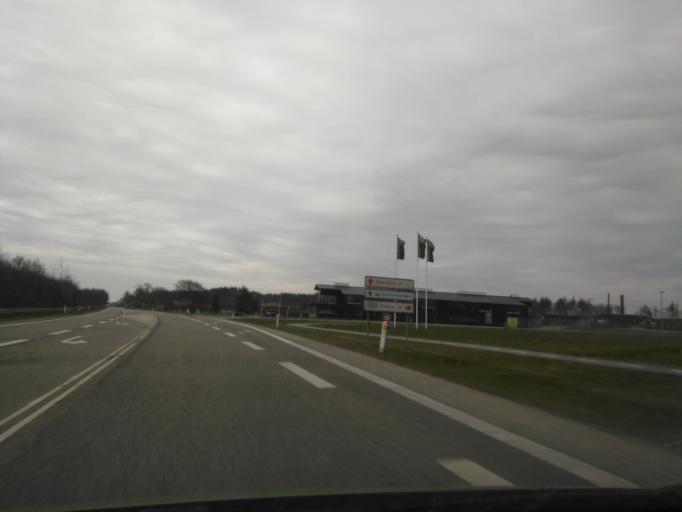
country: DK
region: North Denmark
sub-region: Mariagerfjord Kommune
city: Mariager
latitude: 56.6384
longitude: 9.9758
